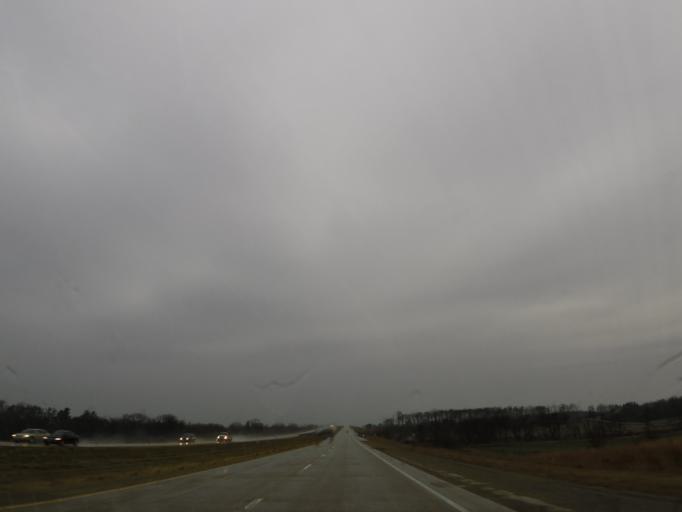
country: US
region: Iowa
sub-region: Floyd County
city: Nora Springs
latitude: 43.1168
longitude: -92.9896
